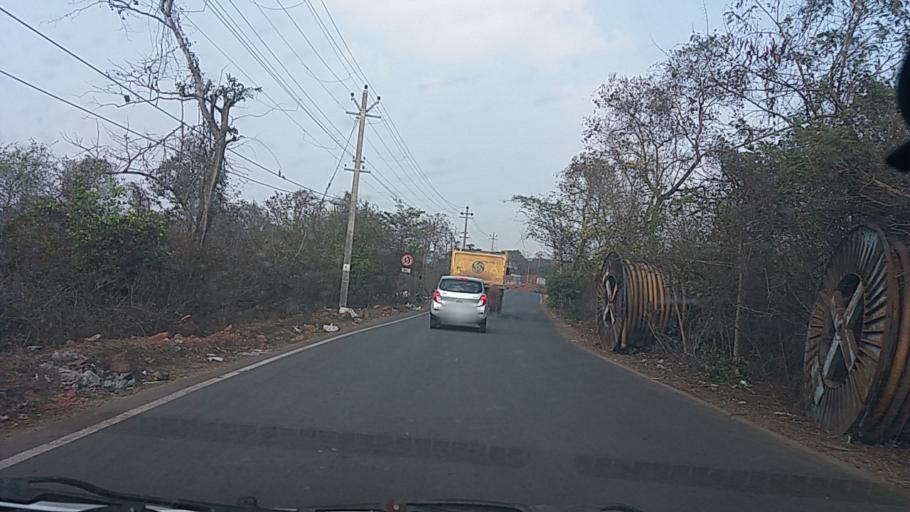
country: IN
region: Goa
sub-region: North Goa
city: Goa Velha
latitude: 15.4880
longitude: 73.9040
